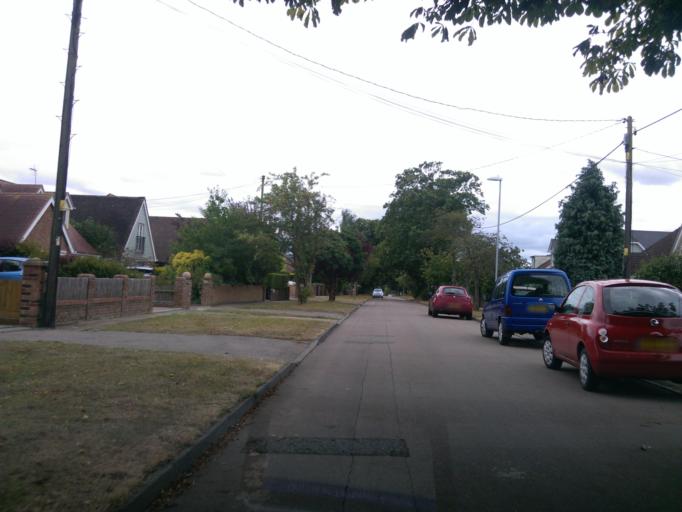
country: GB
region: England
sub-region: Essex
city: West Mersea
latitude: 51.7795
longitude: 0.9290
